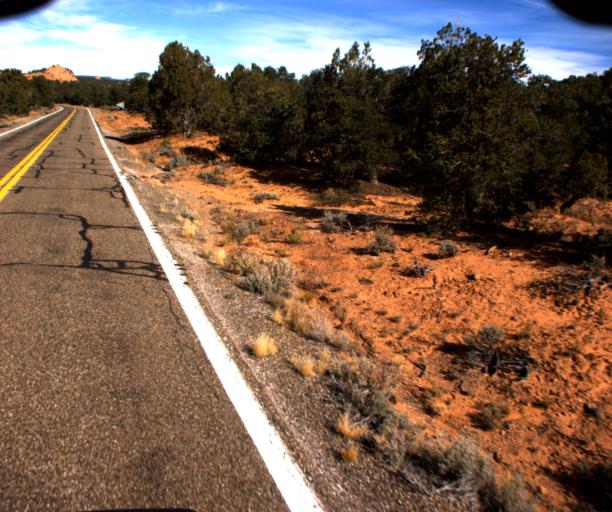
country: US
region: Arizona
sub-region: Navajo County
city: Kayenta
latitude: 36.6507
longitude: -110.5186
